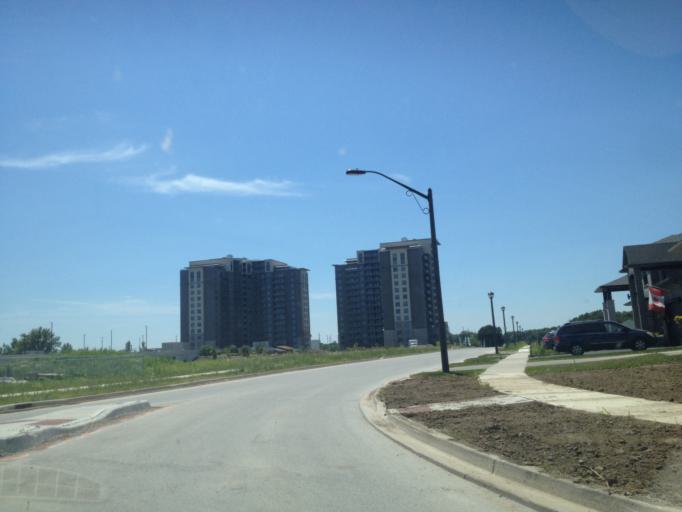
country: CA
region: Ontario
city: London
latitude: 43.0160
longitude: -81.3359
